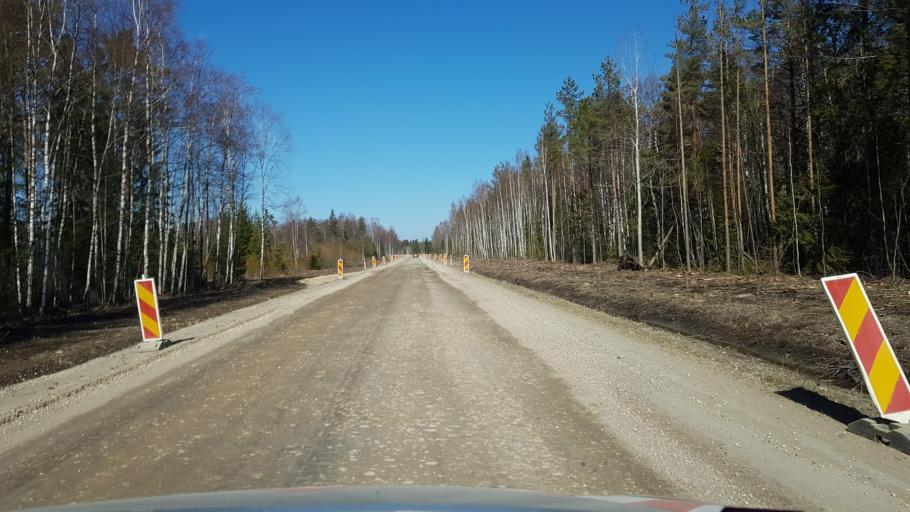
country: EE
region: Laeaene-Virumaa
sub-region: Vinni vald
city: Vinni
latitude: 59.0509
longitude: 26.6552
